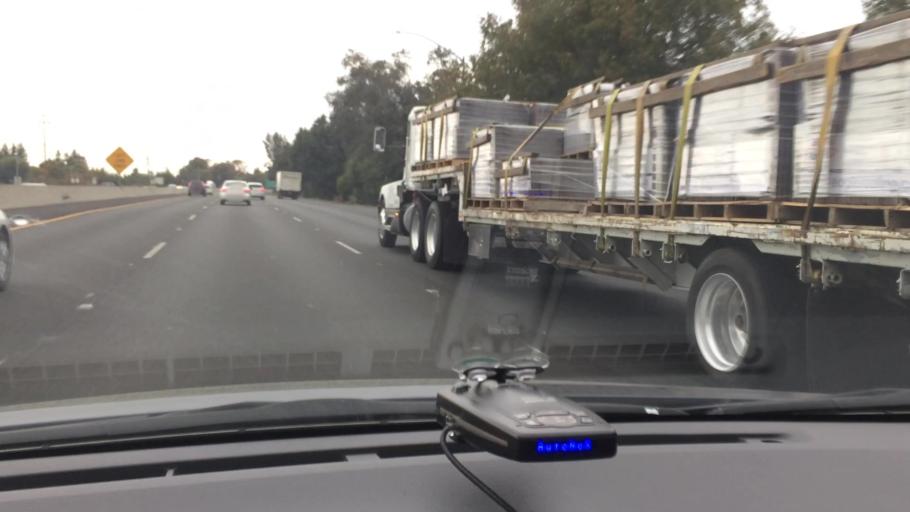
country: US
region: California
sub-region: San Joaquin County
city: Lodi
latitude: 38.1017
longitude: -121.2601
